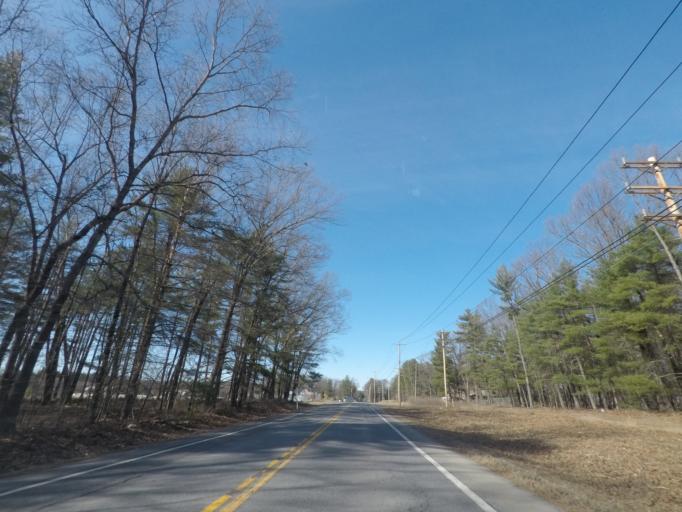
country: US
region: New York
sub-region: Saratoga County
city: Milton
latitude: 43.0570
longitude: -73.8505
